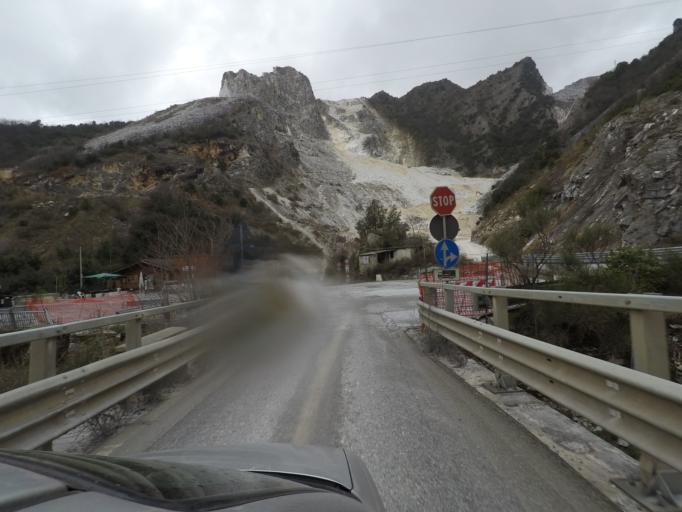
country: IT
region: Tuscany
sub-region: Provincia di Massa-Carrara
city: Massa
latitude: 44.0860
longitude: 10.1276
